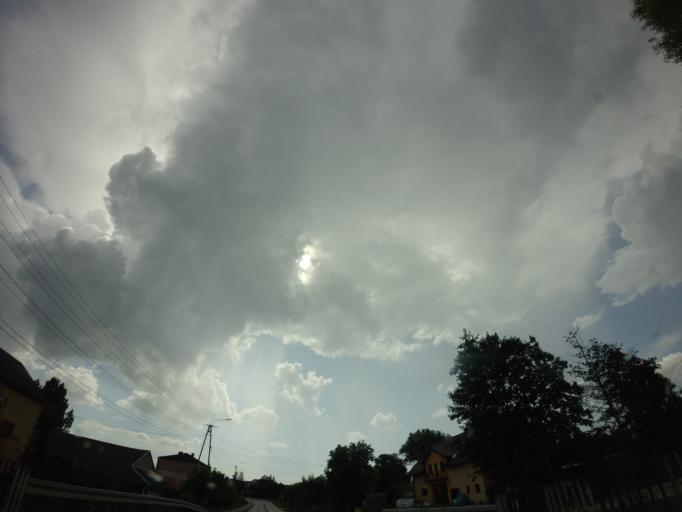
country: PL
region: Swietokrzyskie
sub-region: Powiat buski
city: Solec-Zdroj
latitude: 50.3819
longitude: 20.8973
